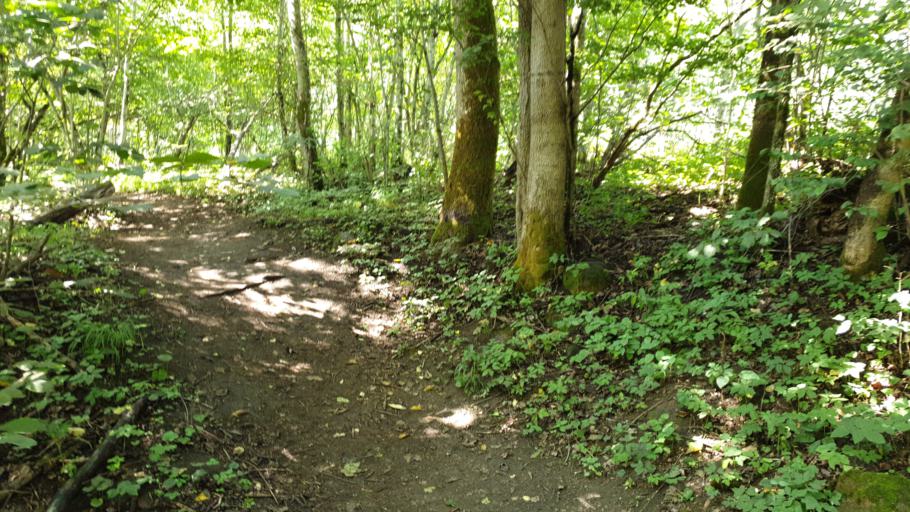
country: LT
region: Vilnius County
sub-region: Vilniaus Rajonas
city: Vievis
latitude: 54.8232
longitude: 24.9385
